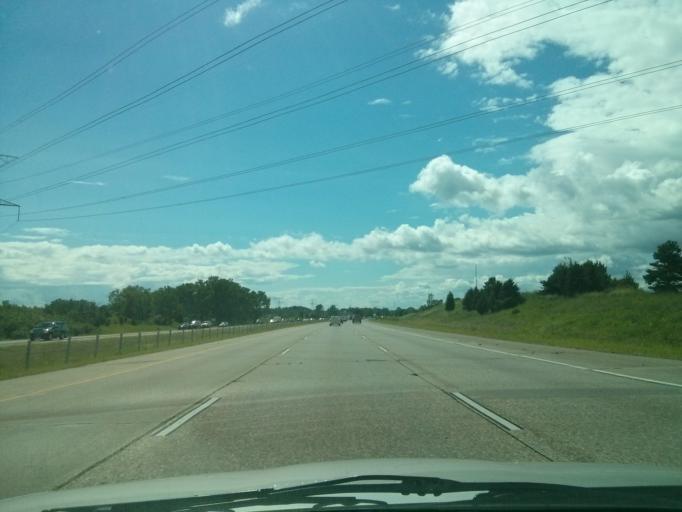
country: US
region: Minnesota
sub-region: Washington County
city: Lakeland
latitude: 44.9497
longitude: -92.8175
